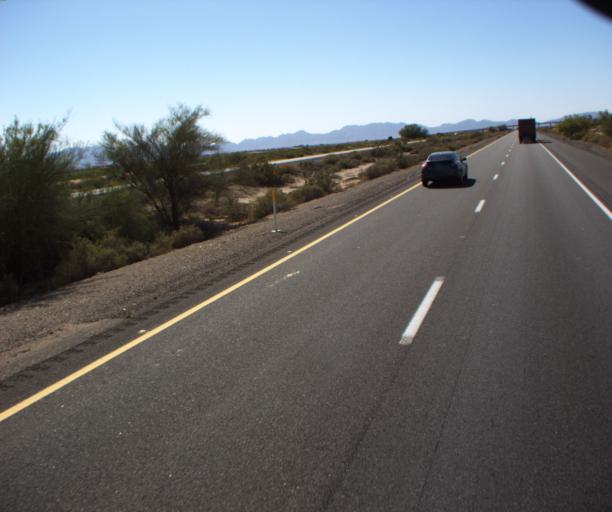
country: US
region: Arizona
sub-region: Yuma County
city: Wellton
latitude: 32.6756
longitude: -114.0611
